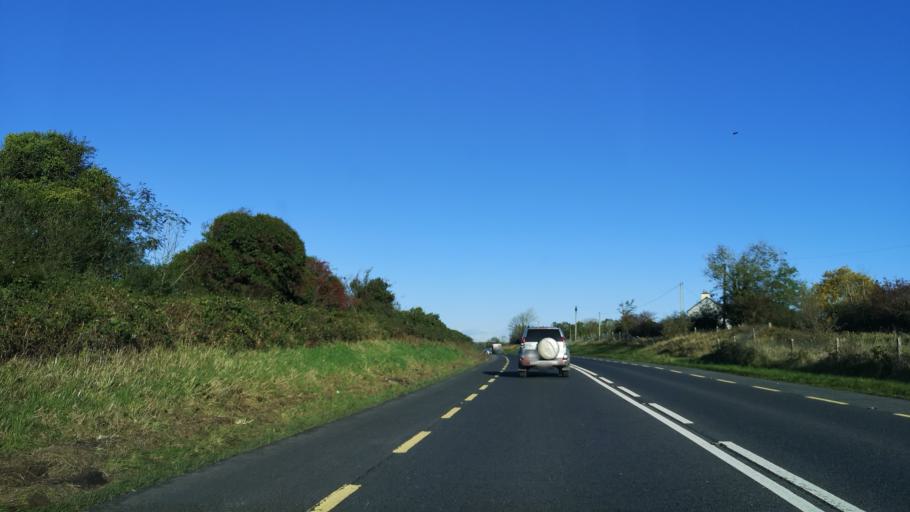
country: IE
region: Connaught
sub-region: County Galway
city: Claregalway
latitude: 53.4071
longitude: -9.0174
